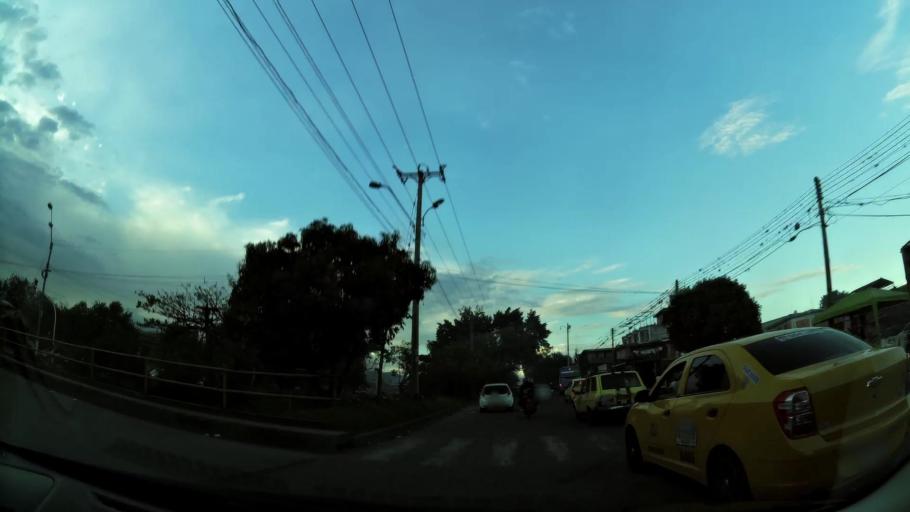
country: CO
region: Valle del Cauca
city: Cali
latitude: 3.4339
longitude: -76.4837
